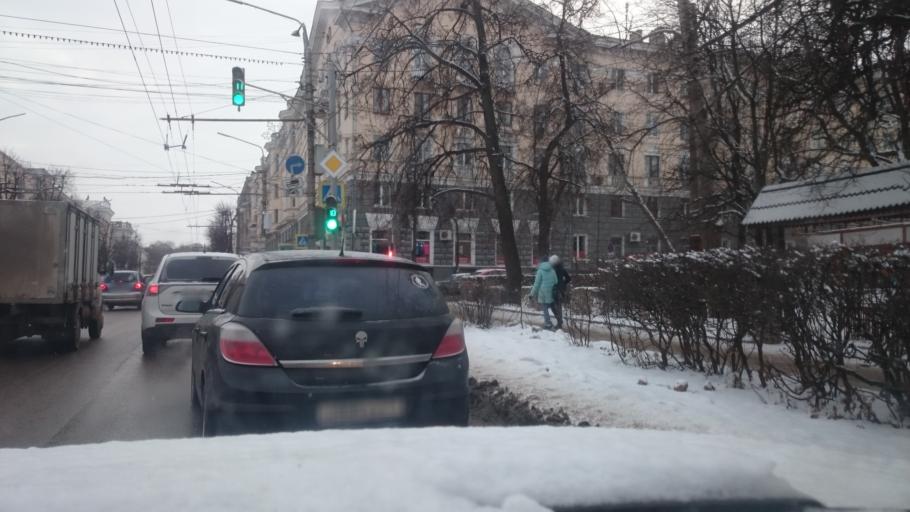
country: RU
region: Tula
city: Tula
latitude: 54.1825
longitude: 37.6011
